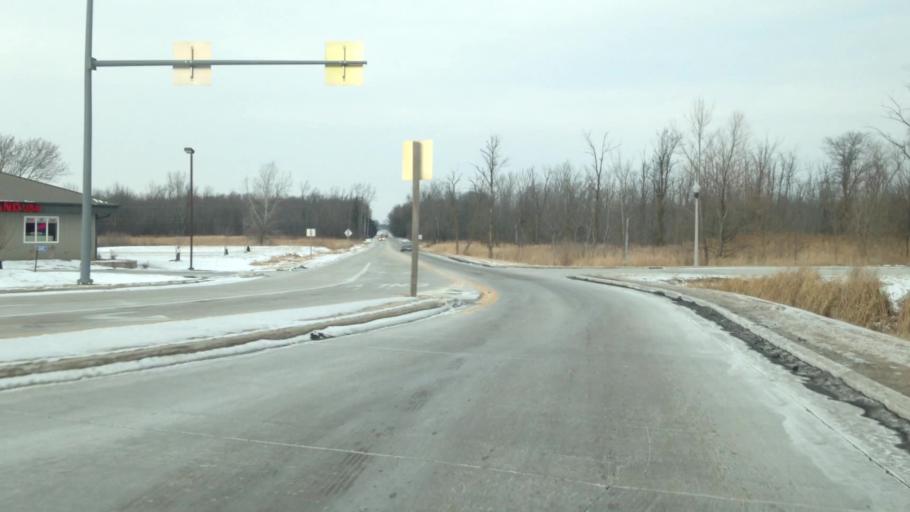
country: US
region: Wisconsin
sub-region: Waukesha County
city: Menomonee Falls
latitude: 43.1964
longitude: -88.1427
